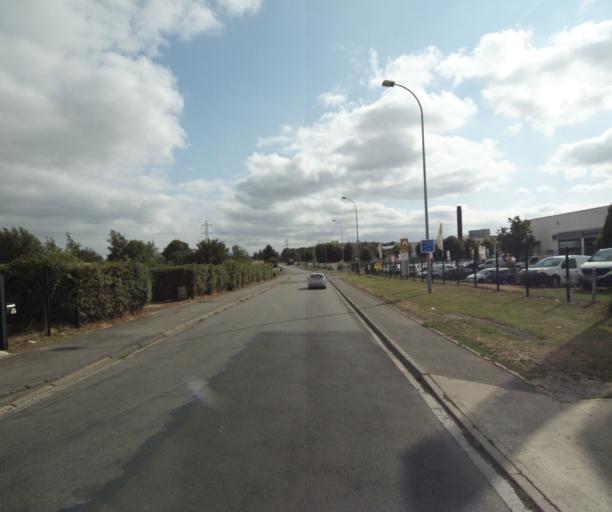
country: FR
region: Nord-Pas-de-Calais
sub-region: Departement du Nord
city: Toufflers
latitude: 50.6701
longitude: 3.2277
